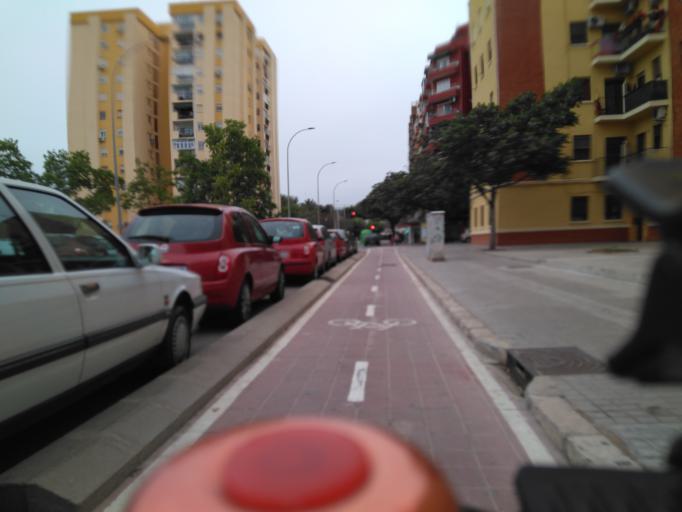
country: ES
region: Valencia
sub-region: Provincia de Valencia
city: Mislata
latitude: 39.4670
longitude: -0.4042
